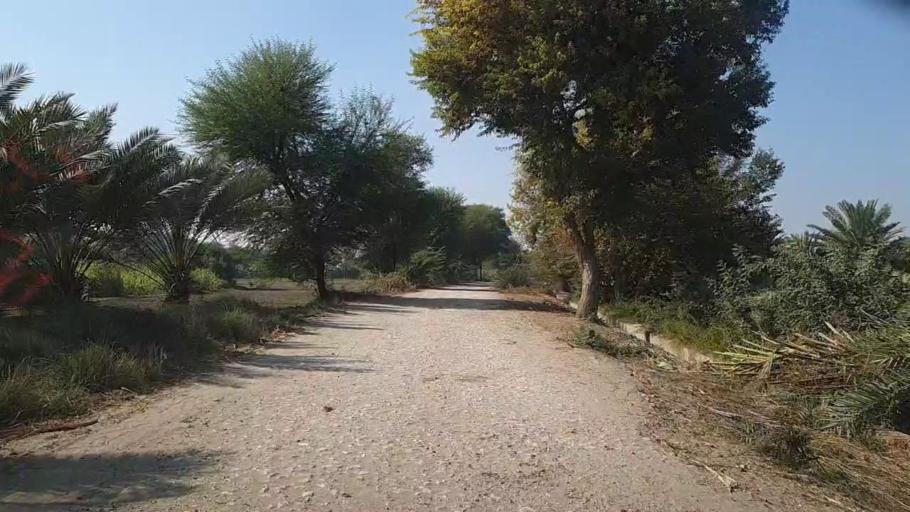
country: PK
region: Sindh
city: Bozdar
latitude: 27.1944
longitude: 68.6678
